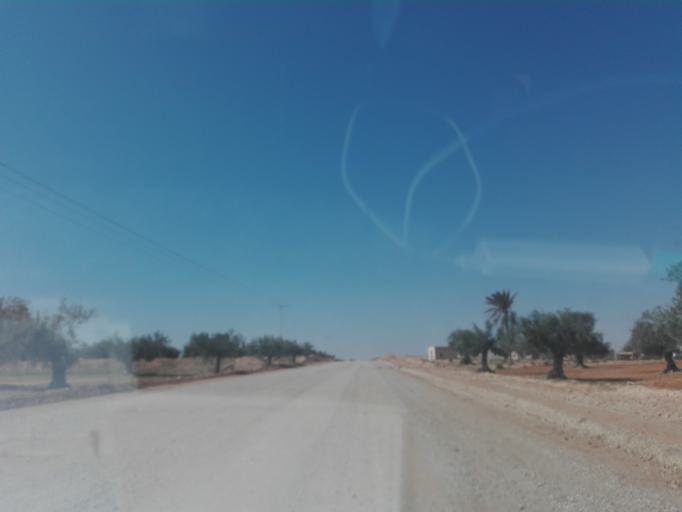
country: TN
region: Safaqis
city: Sfax
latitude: 34.6850
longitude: 10.4605
